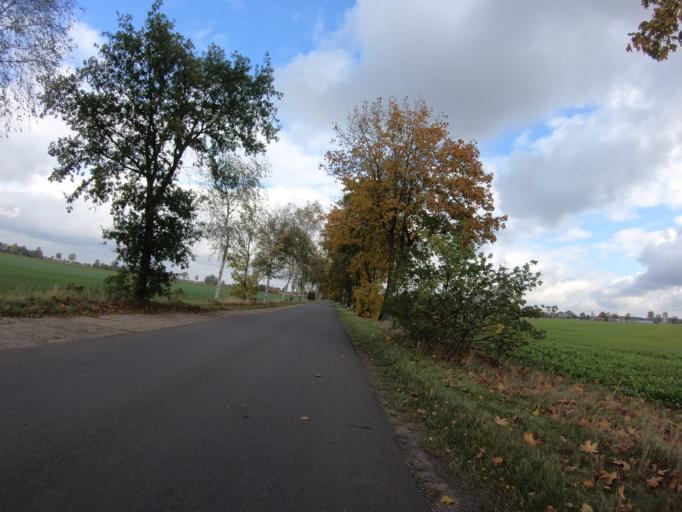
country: DE
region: Lower Saxony
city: Wahrenholz
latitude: 52.6030
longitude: 10.5907
